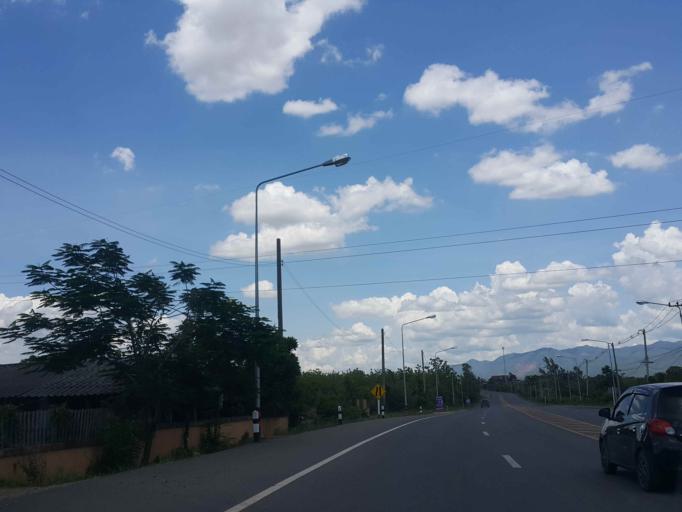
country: TH
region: Phrae
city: Nong Muang Khai
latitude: 18.2039
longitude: 100.2119
